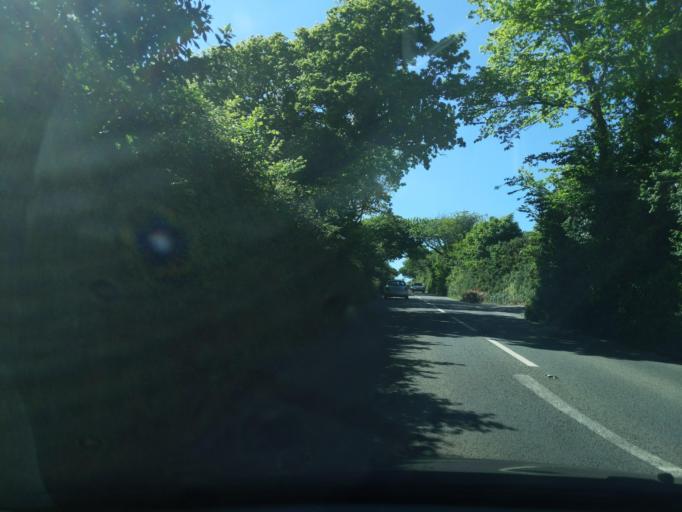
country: GB
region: England
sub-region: Cornwall
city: Helston
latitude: 50.1054
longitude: -5.2911
